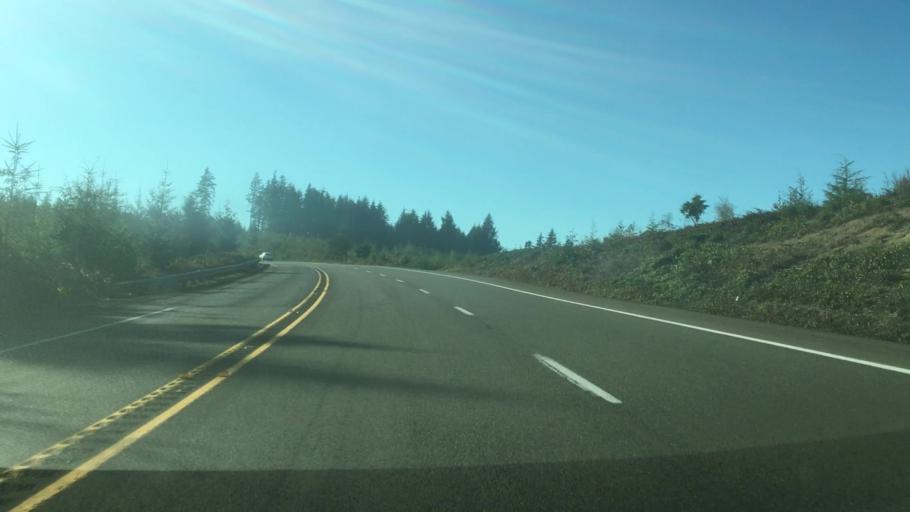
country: US
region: Washington
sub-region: Pacific County
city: South Bend
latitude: 46.6857
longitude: -123.8831
